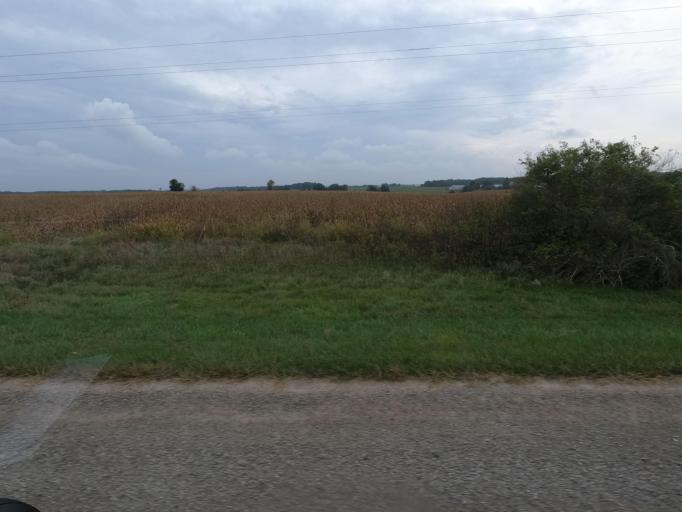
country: US
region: Iowa
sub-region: Van Buren County
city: Keosauqua
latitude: 40.8436
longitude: -92.0207
